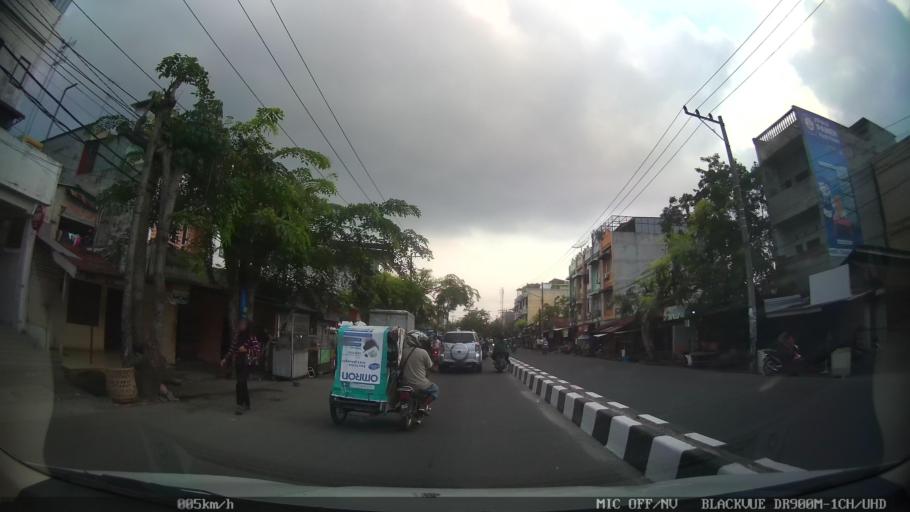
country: ID
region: North Sumatra
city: Medan
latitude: 3.5961
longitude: 98.7117
